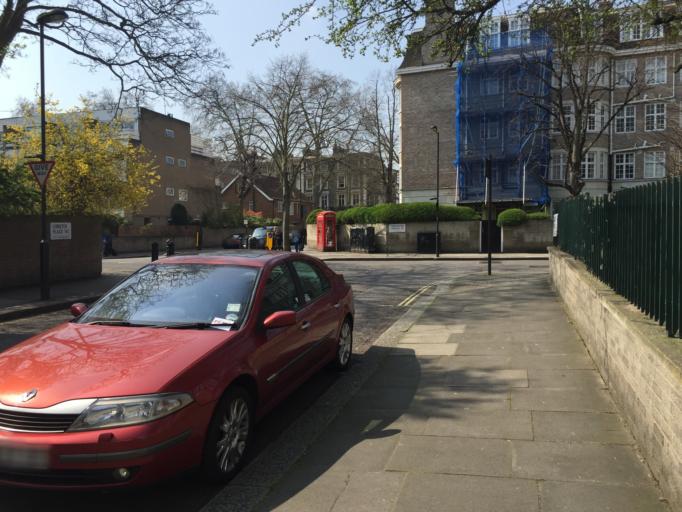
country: GB
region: England
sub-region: Greater London
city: Bayswater
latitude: 51.5143
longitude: -0.1846
